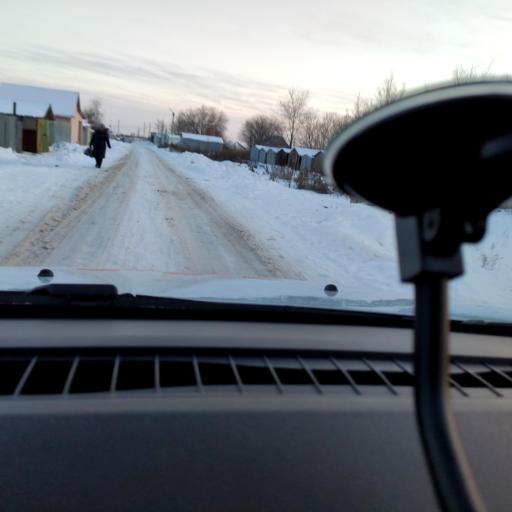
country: RU
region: Samara
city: Dubovyy Umet
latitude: 53.0800
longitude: 50.2255
